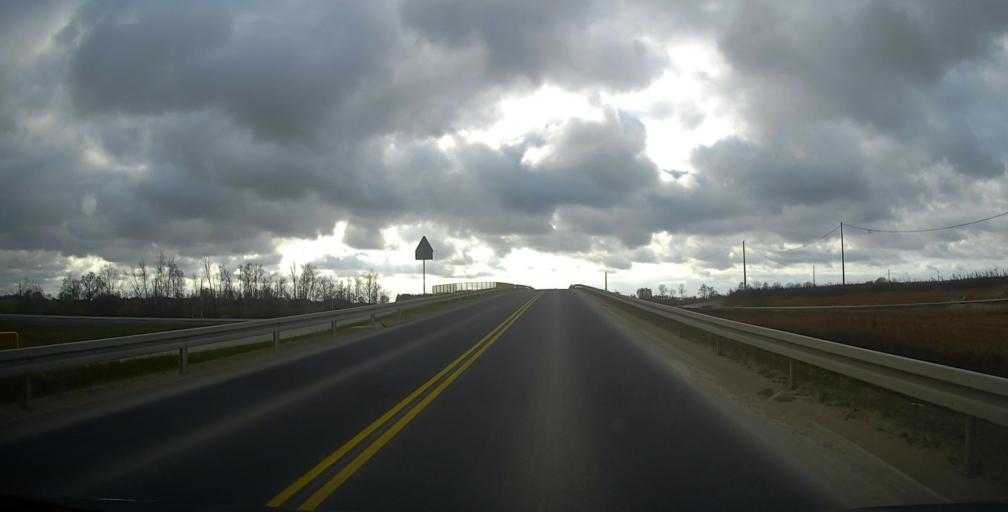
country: PL
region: Warmian-Masurian Voivodeship
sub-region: Powiat elcki
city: Elk
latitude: 53.8560
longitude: 22.4975
